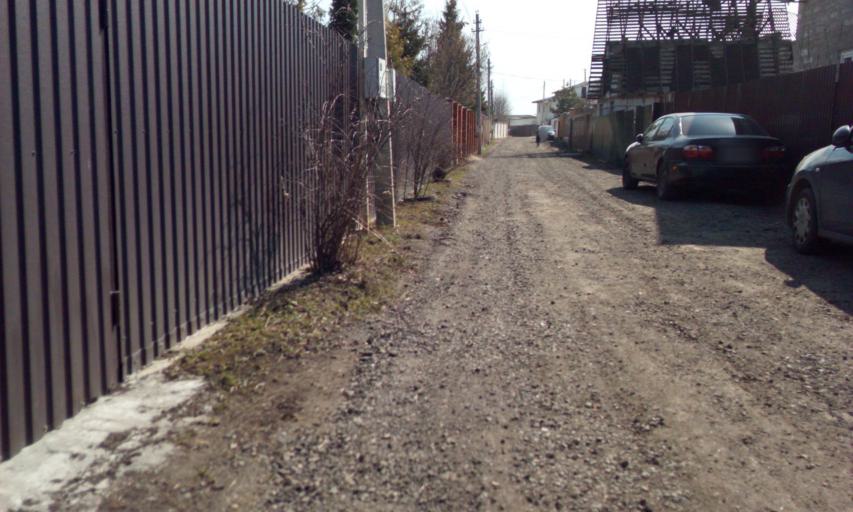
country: RU
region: Moskovskaya
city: Kommunarka
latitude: 55.5206
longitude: 37.4580
